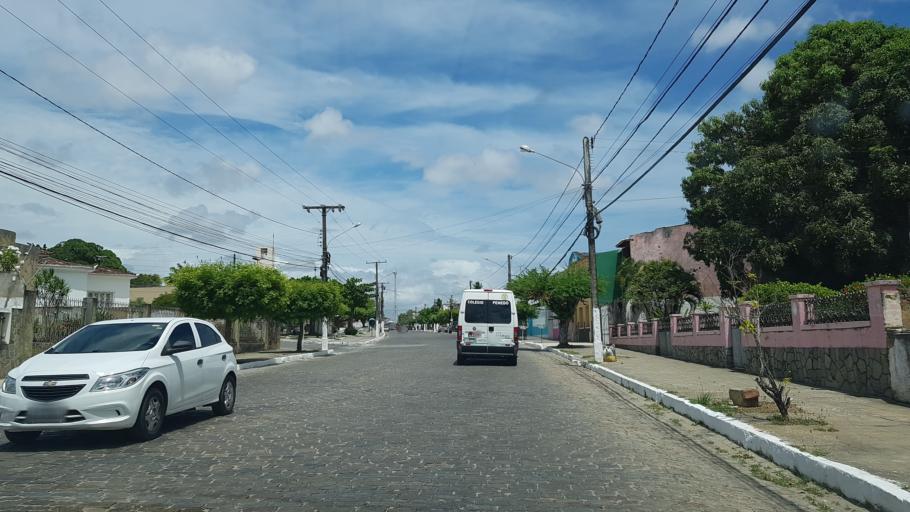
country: BR
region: Alagoas
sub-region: Penedo
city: Penedo
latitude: -10.2859
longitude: -36.5764
